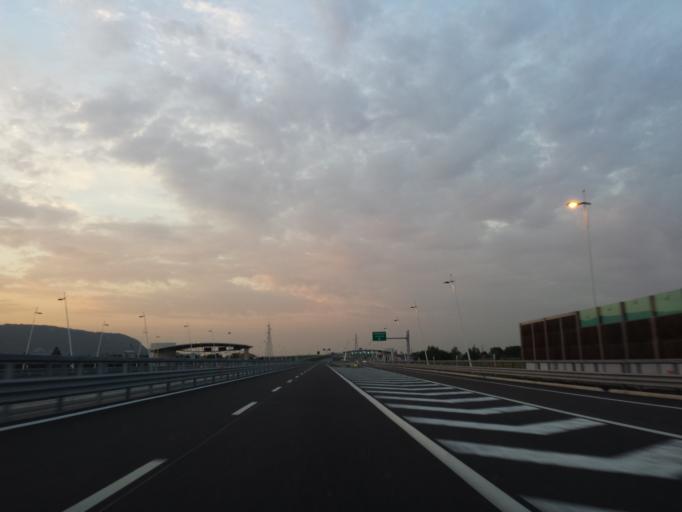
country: IT
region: Veneto
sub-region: Provincia di Vicenza
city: Villaganzerla
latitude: 45.4460
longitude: 11.6318
